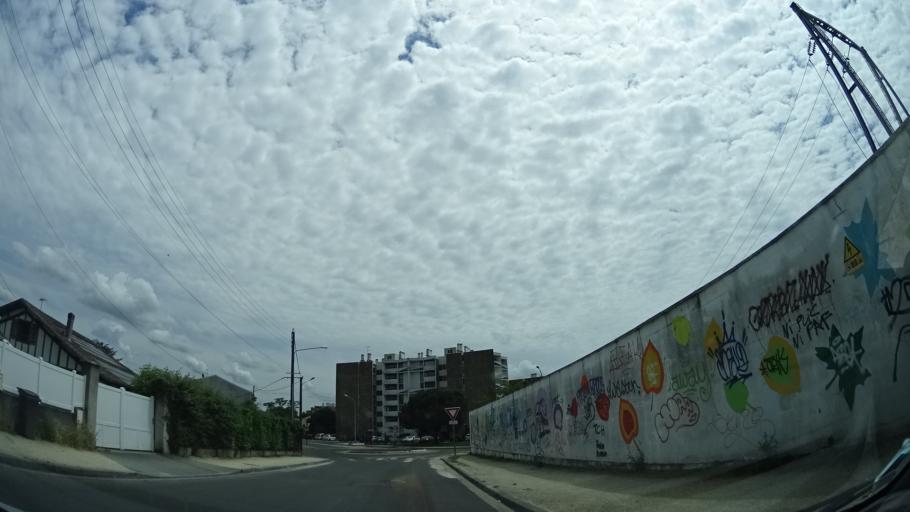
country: FR
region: Aquitaine
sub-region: Departement de la Gironde
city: Talence
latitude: 44.7966
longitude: -0.6100
